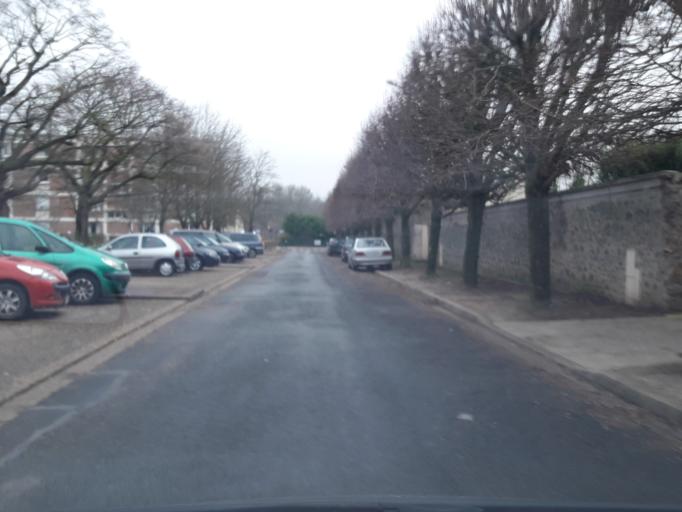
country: FR
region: Ile-de-France
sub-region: Departement de l'Essonne
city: Vert-le-Petit
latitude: 48.5564
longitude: 2.3712
